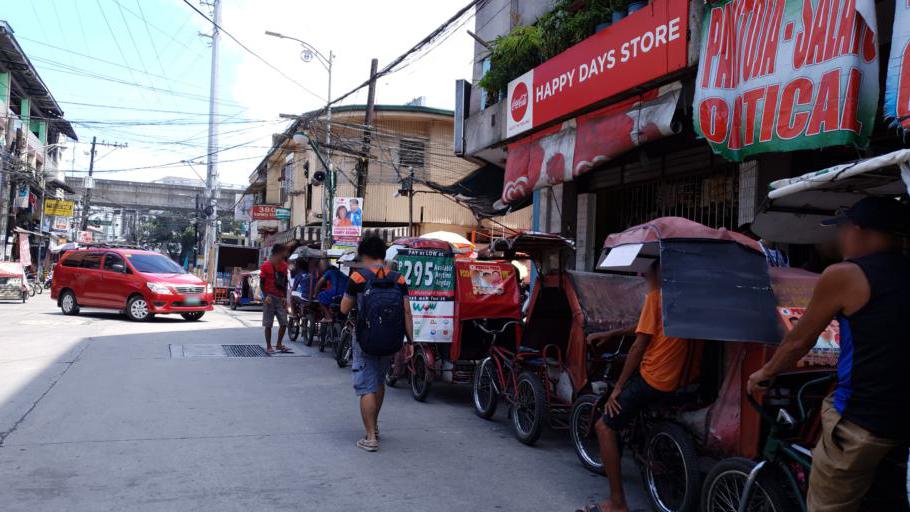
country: PH
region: Metro Manila
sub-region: City of Manila
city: Quiapo
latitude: 14.6008
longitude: 121.0046
